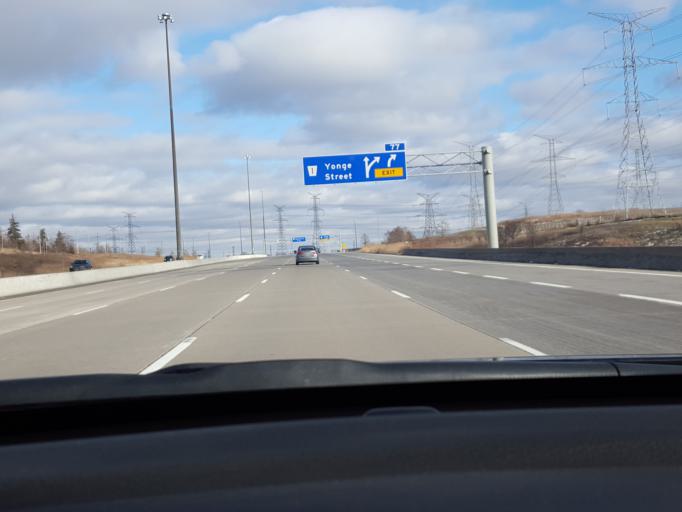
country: CA
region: Ontario
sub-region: York
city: Richmond Hill
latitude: 43.8307
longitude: -79.4397
